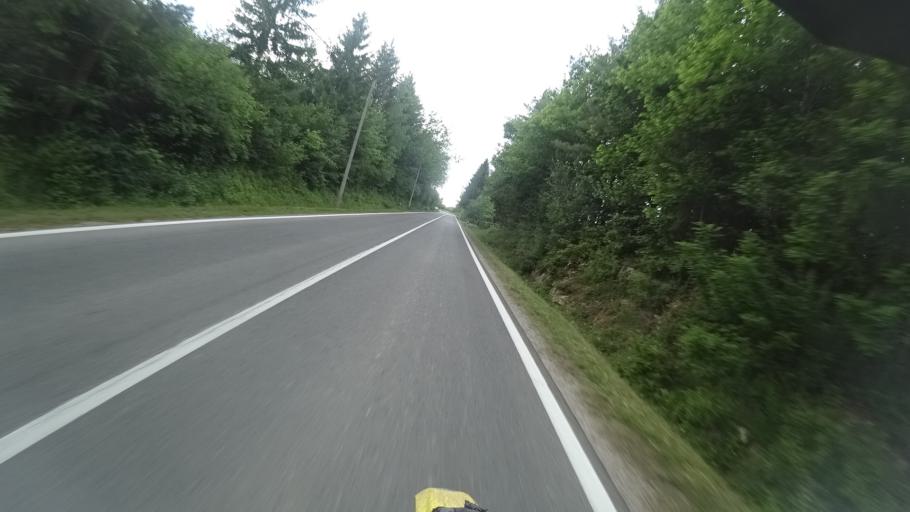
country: HR
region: Licko-Senjska
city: Gospic
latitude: 44.4955
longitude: 15.4594
